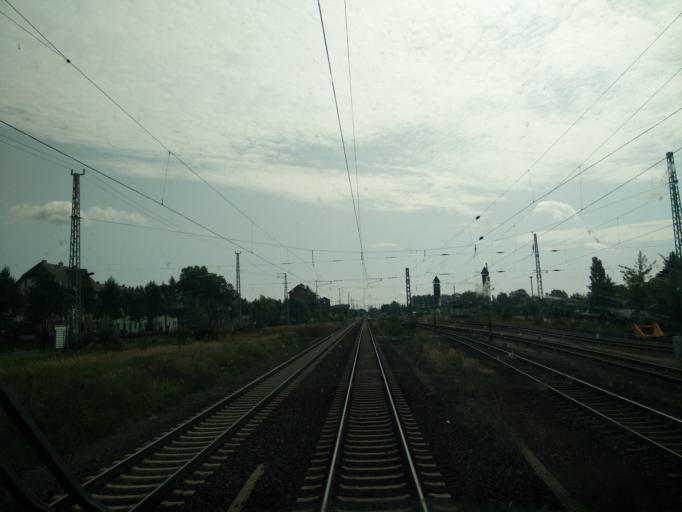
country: DE
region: Brandenburg
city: Lubbenau
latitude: 51.8644
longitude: 13.9553
